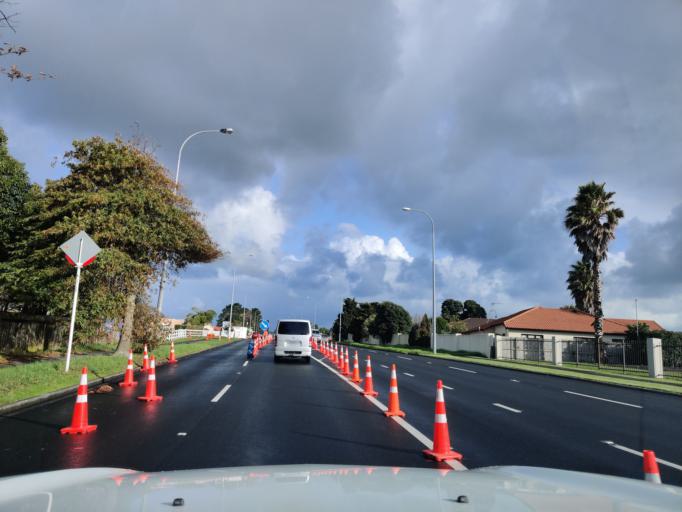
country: NZ
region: Auckland
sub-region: Auckland
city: Pakuranga
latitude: -36.9199
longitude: 174.9130
